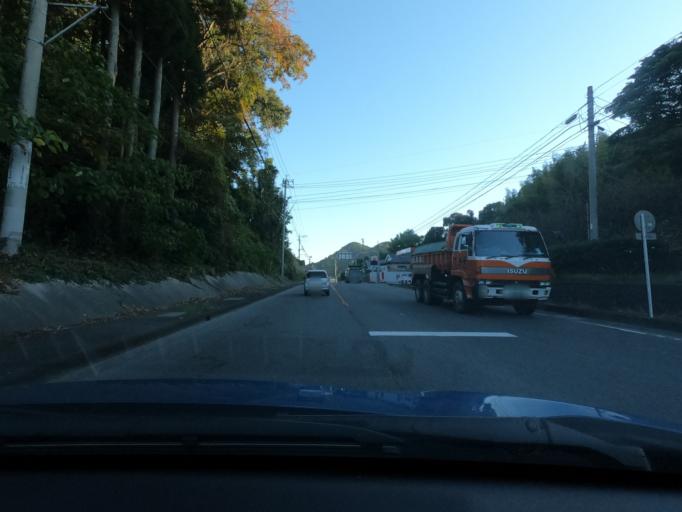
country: JP
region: Kagoshima
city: Satsumasendai
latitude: 31.8581
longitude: 130.2318
